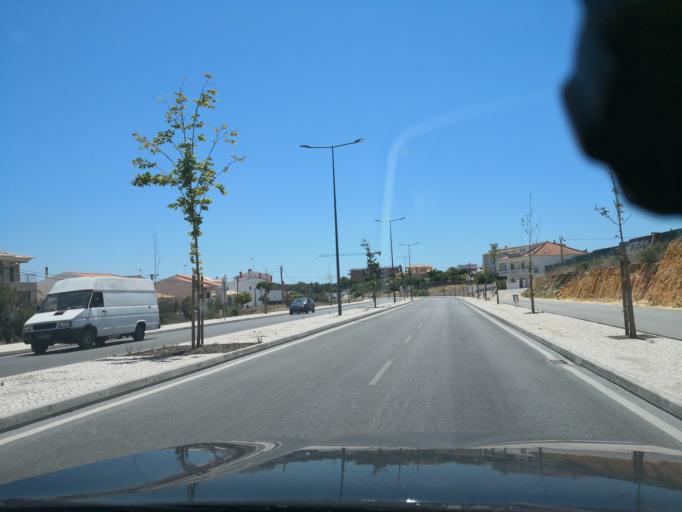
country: PT
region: Faro
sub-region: Loule
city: Quarteira
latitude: 37.0722
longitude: -8.0877
